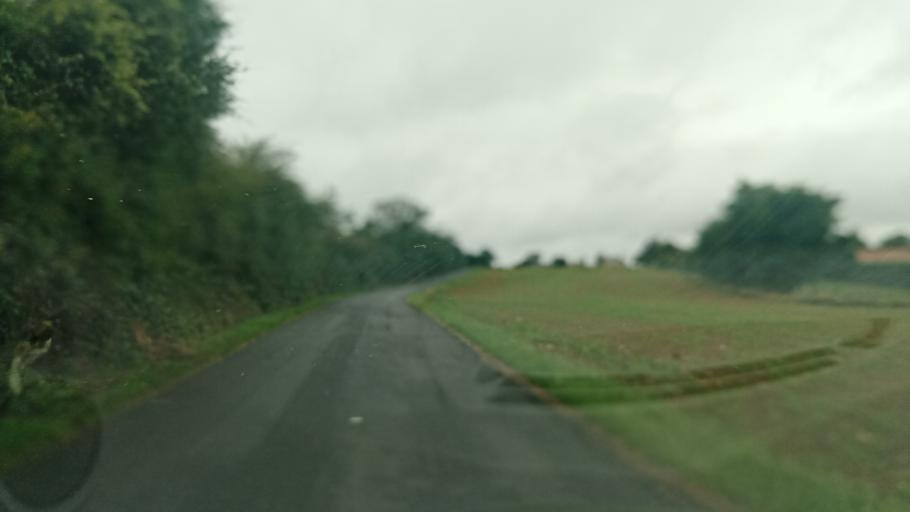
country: FR
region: Poitou-Charentes
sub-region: Departement de la Vienne
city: Vouneuil-sous-Biard
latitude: 46.5932
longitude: 0.2828
